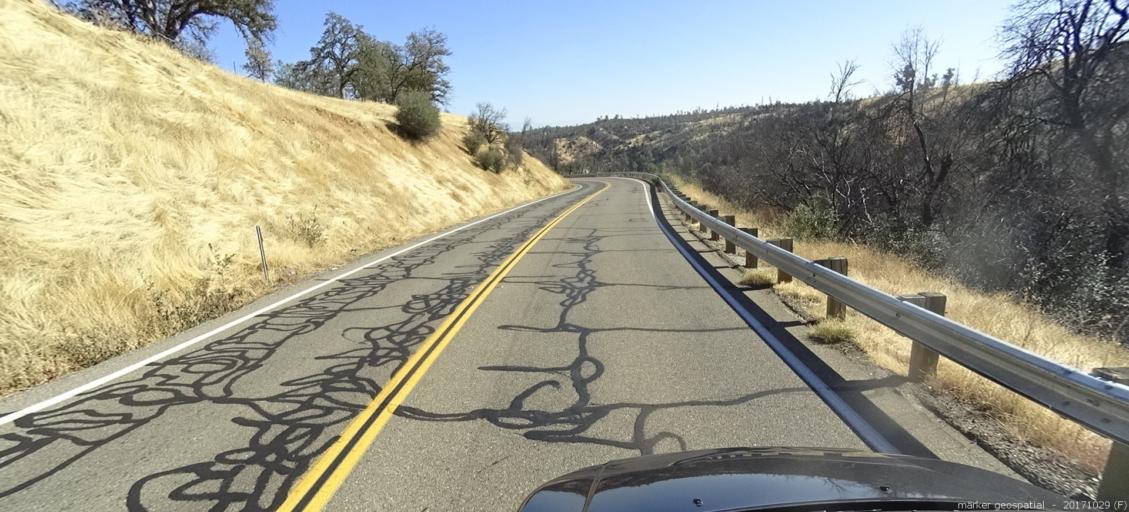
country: US
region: California
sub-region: Shasta County
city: Shasta
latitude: 40.4923
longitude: -122.5103
